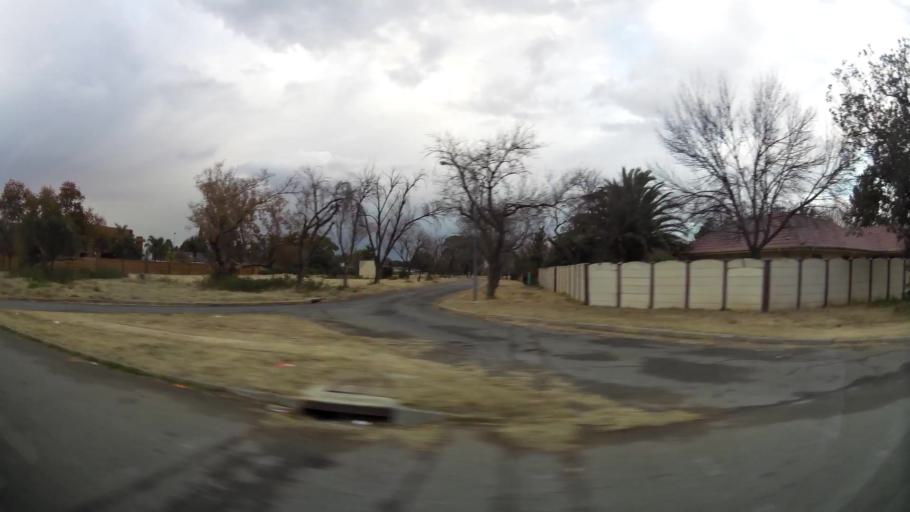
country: ZA
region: Orange Free State
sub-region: Lejweleputswa District Municipality
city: Welkom
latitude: -27.9585
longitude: 26.7368
